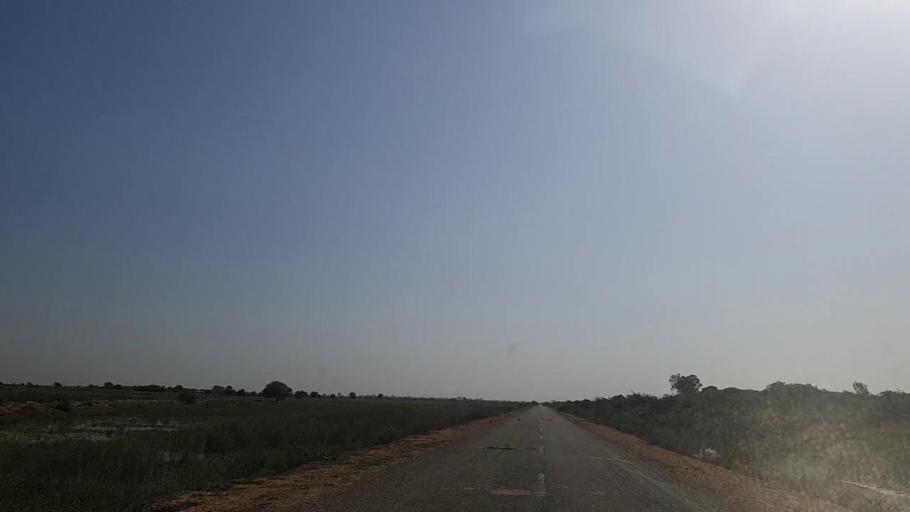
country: PK
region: Sindh
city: Jati
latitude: 24.4511
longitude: 68.2636
